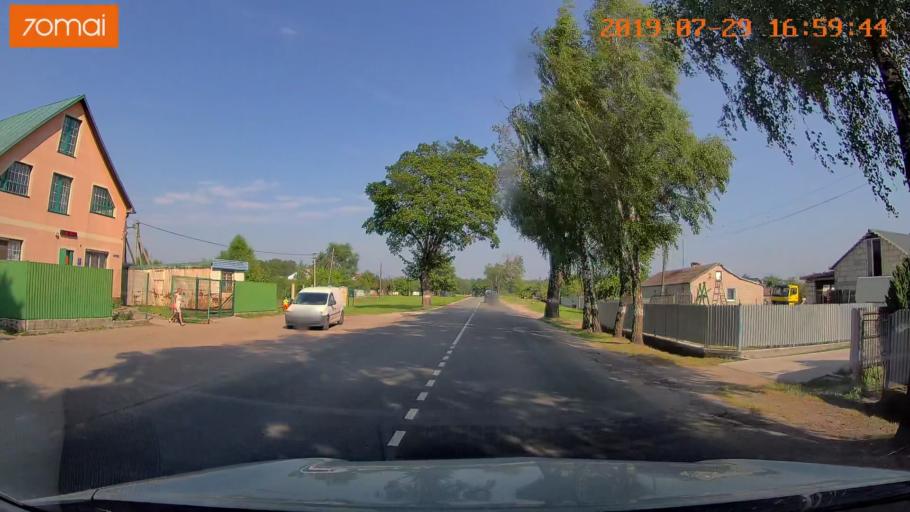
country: RU
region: Kaliningrad
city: Volochayevskoye
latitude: 54.8196
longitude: 20.2159
